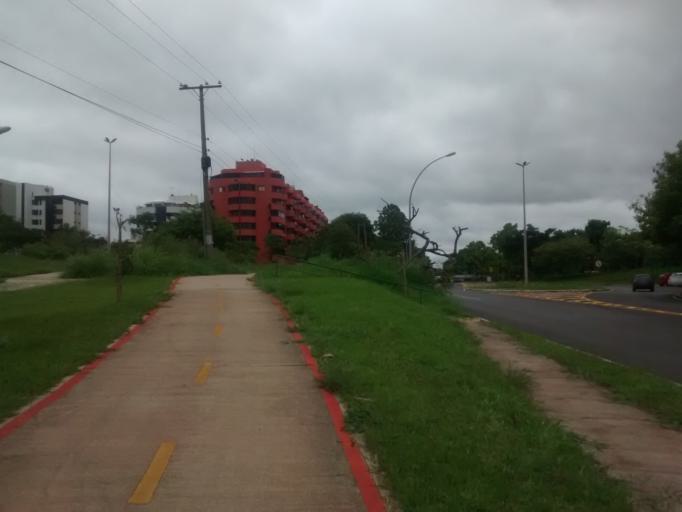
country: BR
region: Federal District
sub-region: Brasilia
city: Brasilia
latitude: -15.7423
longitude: -47.8870
